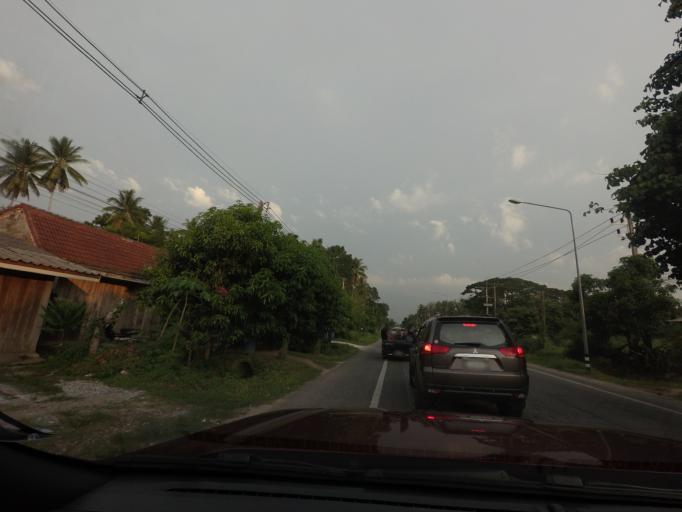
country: TH
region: Pattani
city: Mae Lan
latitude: 6.5979
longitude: 101.1945
